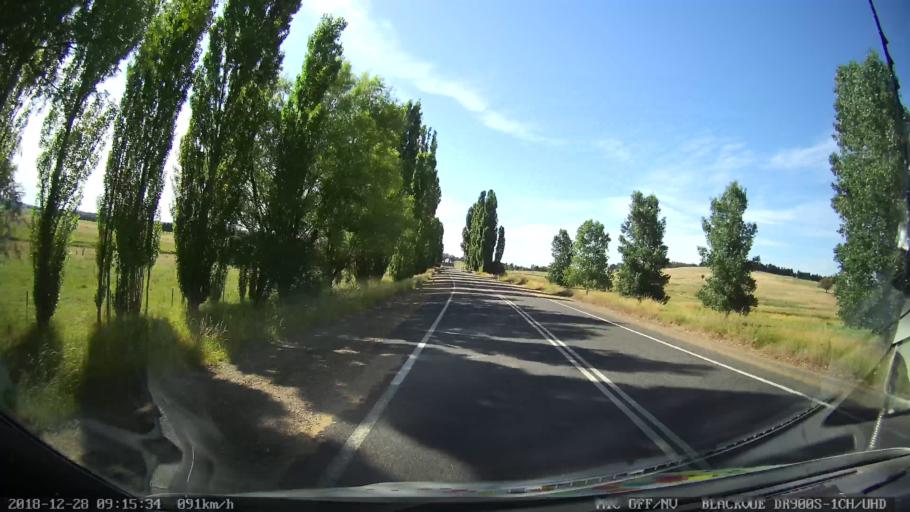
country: AU
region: New South Wales
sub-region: Upper Lachlan Shire
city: Crookwell
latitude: -34.2979
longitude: 149.3498
